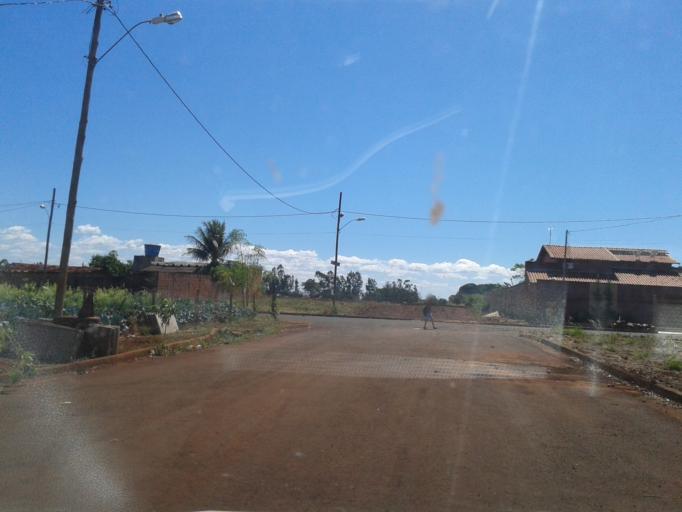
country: BR
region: Minas Gerais
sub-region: Centralina
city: Centralina
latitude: -18.5944
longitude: -49.2023
